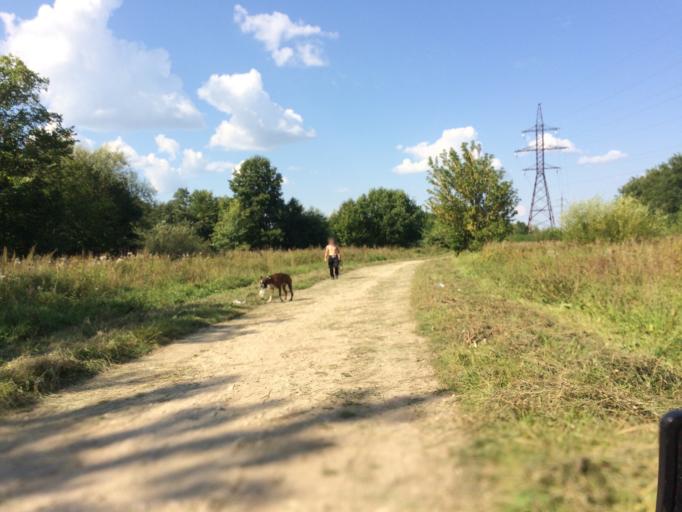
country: RU
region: Mariy-El
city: Yoshkar-Ola
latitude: 56.6136
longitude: 47.9318
